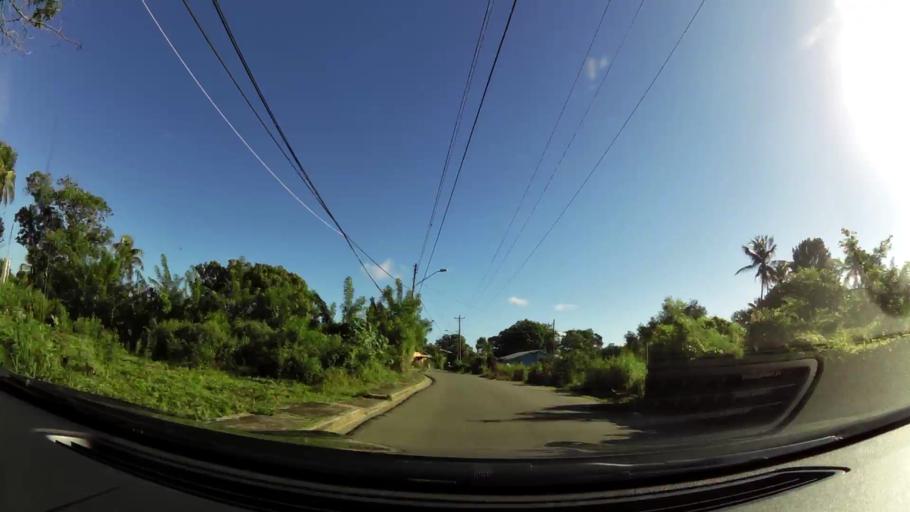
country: TT
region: Tobago
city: Scarborough
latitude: 11.1524
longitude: -60.8318
